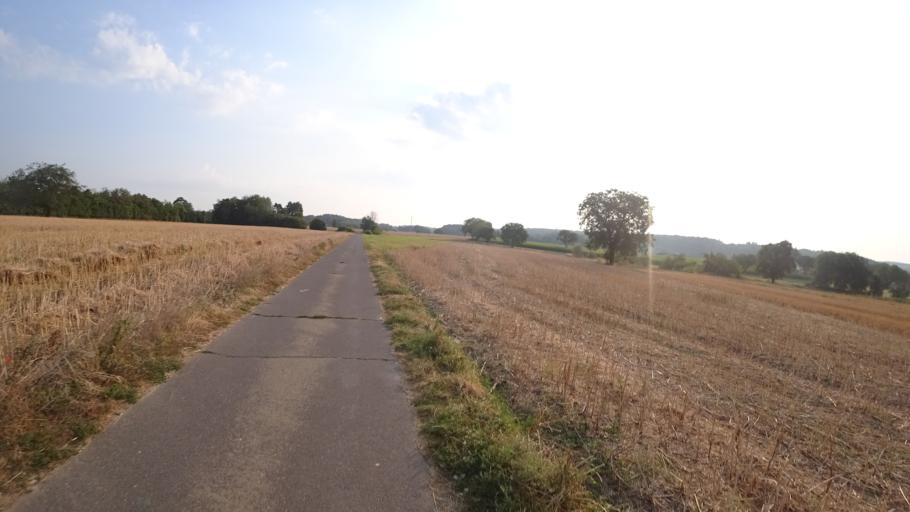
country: DE
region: Rheinland-Pfalz
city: Weitersburg
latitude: 50.4219
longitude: 7.6166
